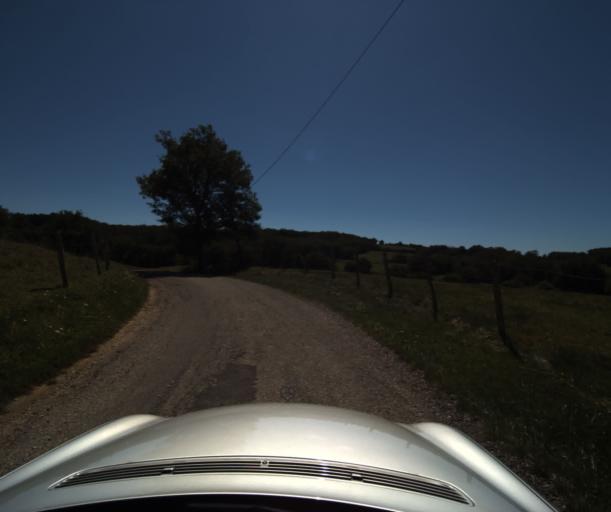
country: FR
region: Midi-Pyrenees
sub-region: Departement de l'Ariege
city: Belesta
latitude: 42.9792
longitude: 1.9229
